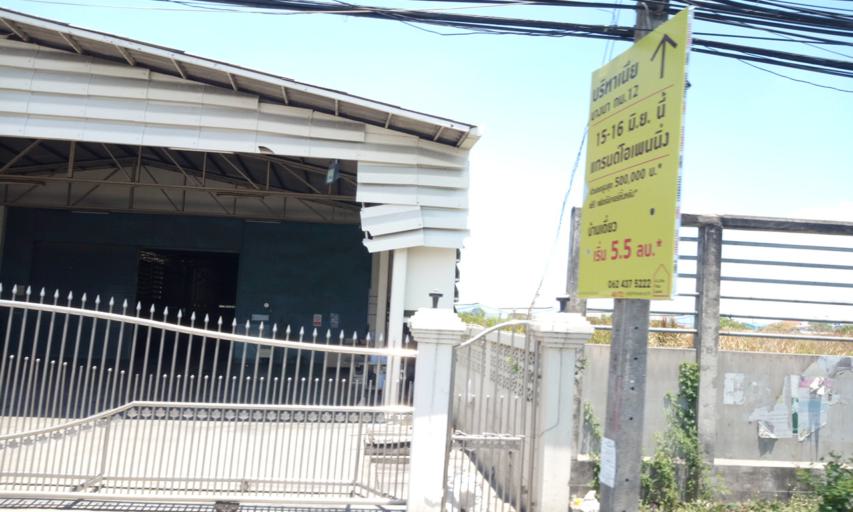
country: TH
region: Bangkok
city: Bang Na
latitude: 13.6178
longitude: 100.7040
